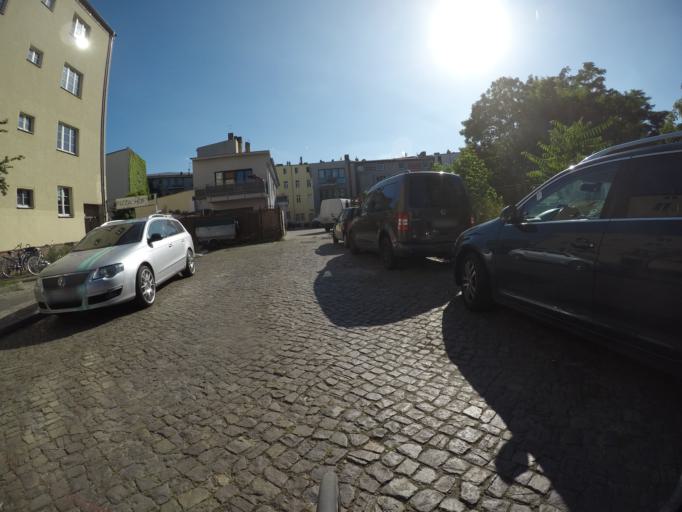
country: DE
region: Berlin
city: Oberschoneweide
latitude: 52.4631
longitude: 13.5153
